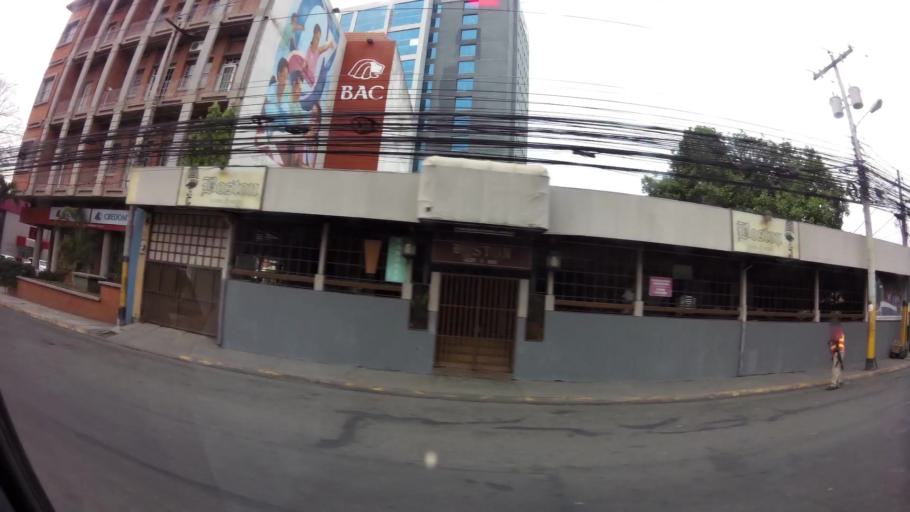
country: HN
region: Francisco Morazan
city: Tegucigalpa
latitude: 14.1002
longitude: -87.1867
